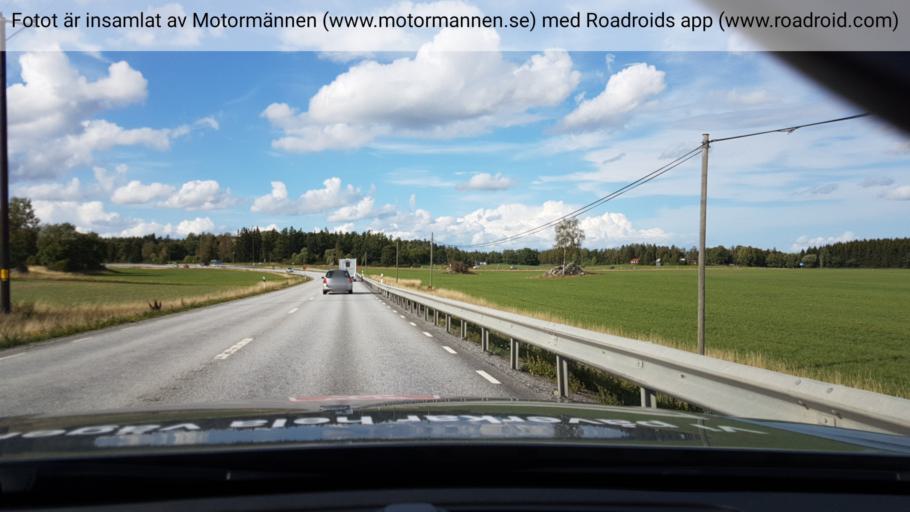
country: SE
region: Uppsala
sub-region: Habo Kommun
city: Balsta
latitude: 59.6283
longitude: 17.6016
